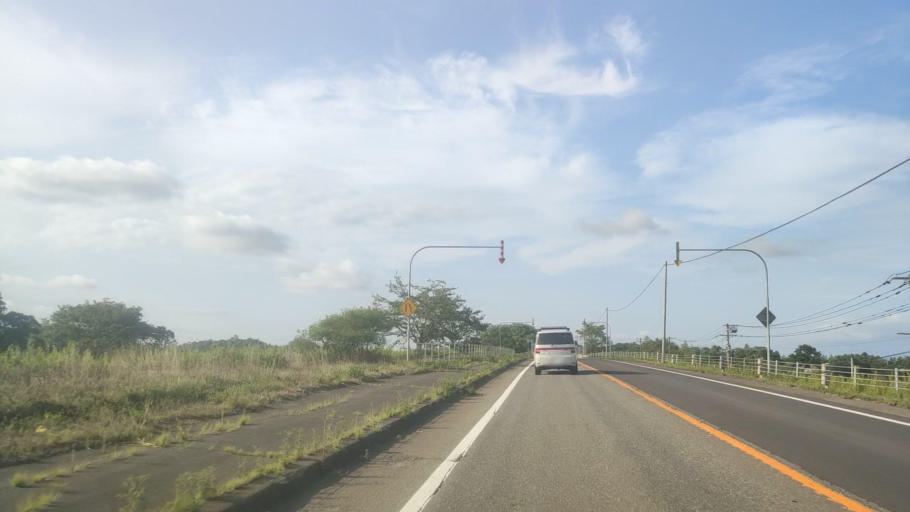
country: JP
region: Hokkaido
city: Chitose
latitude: 42.8871
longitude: 141.8122
